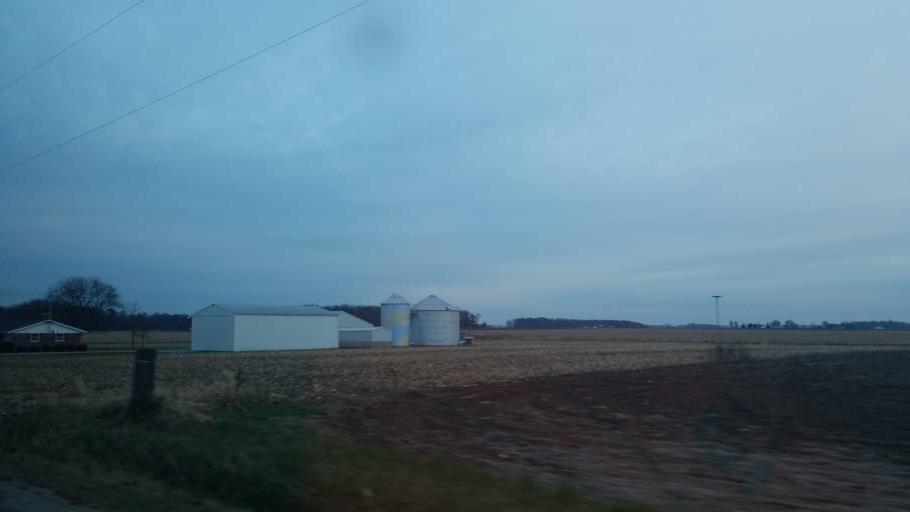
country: US
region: Indiana
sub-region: Adams County
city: Decatur
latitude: 40.7883
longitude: -84.9612
